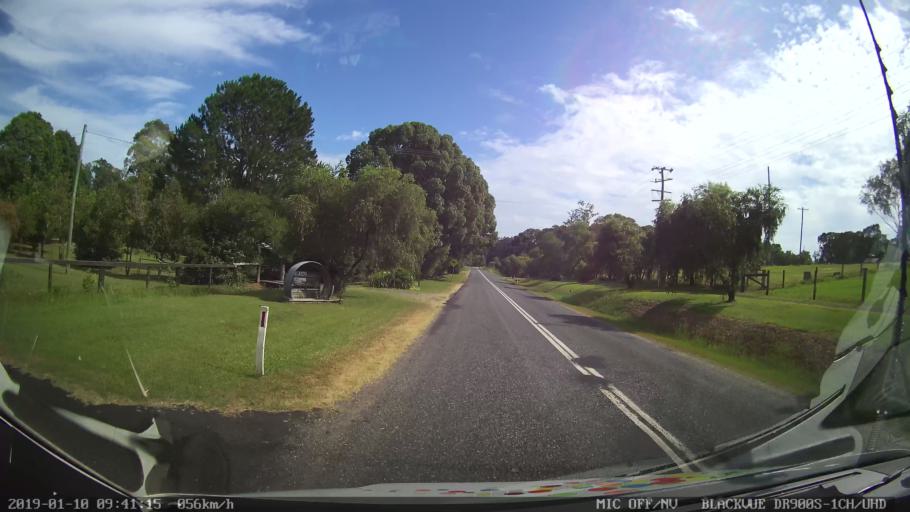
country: AU
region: New South Wales
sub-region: Coffs Harbour
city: Nana Glen
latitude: -30.1437
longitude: 153.0076
